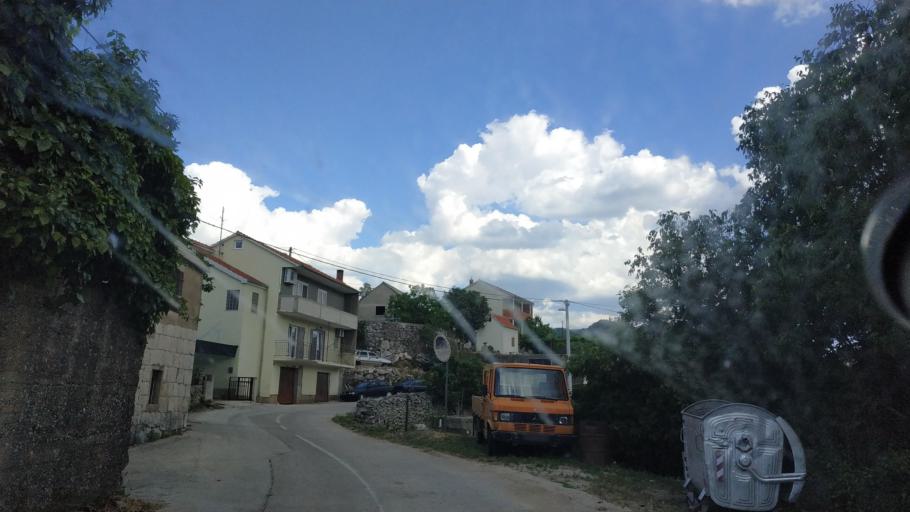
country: HR
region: Splitsko-Dalmatinska
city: Dugopolje
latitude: 43.5644
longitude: 16.6533
